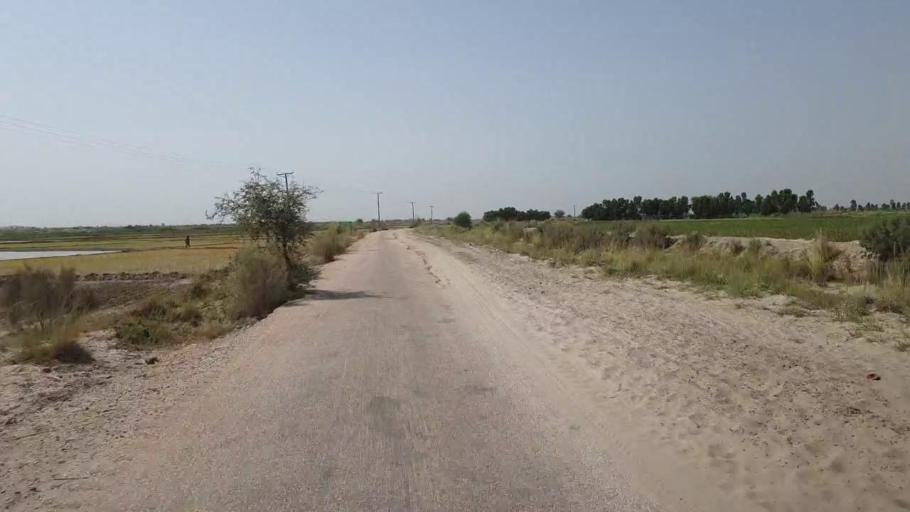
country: PK
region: Sindh
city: Jam Sahib
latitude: 26.4182
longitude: 68.9081
